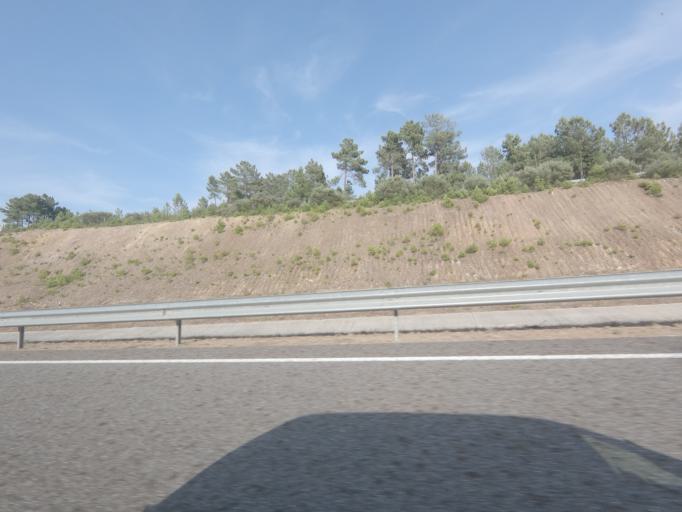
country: ES
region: Galicia
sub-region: Provincia de Ourense
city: Oimbra
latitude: 41.8861
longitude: -7.4269
